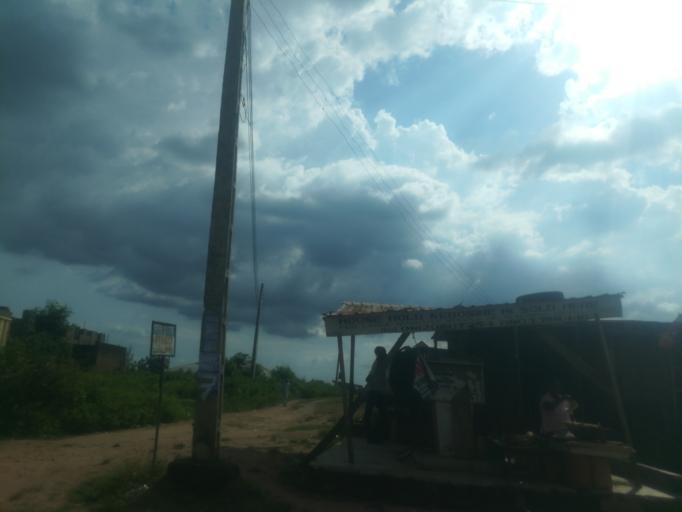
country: NG
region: Oyo
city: Ibadan
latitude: 7.4098
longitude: 3.8238
